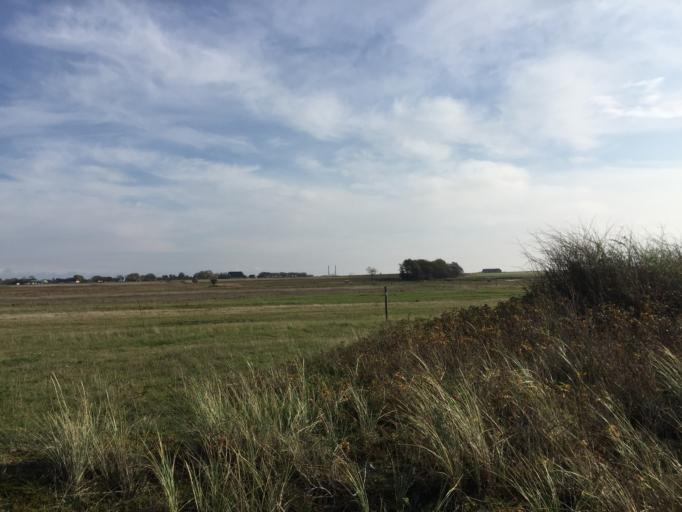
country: DK
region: Zealand
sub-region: Slagelse Kommune
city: Korsor
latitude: 55.2089
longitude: 11.1732
